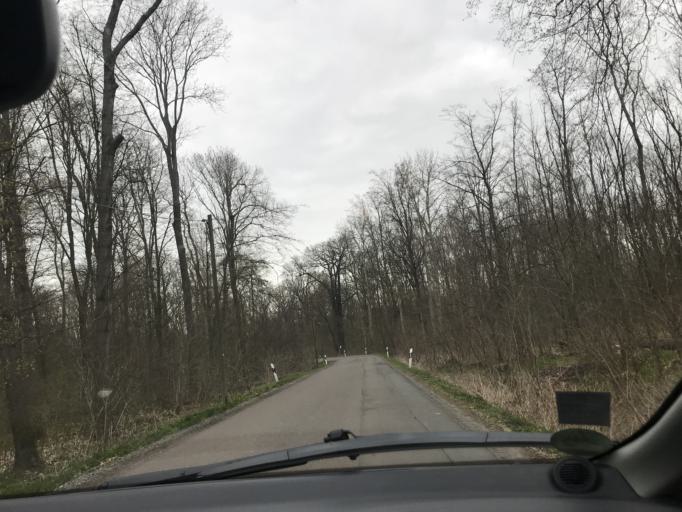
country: DE
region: Saxony
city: Schkeuditz
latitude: 51.3677
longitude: 12.2566
